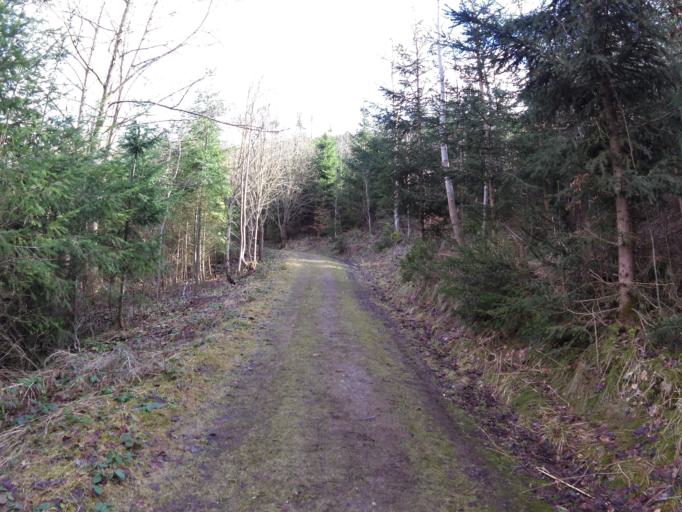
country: DE
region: Thuringia
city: Ilmenau
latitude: 50.6723
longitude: 10.9130
